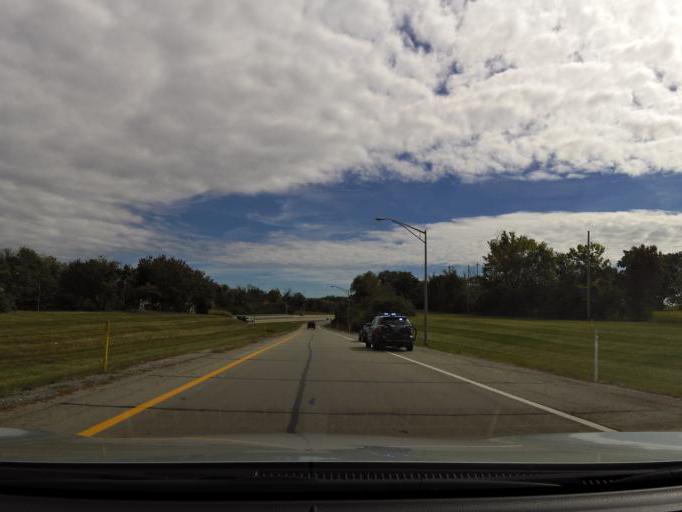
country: US
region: Ohio
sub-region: Hamilton County
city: Delhi Hills
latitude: 39.0695
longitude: -84.6538
